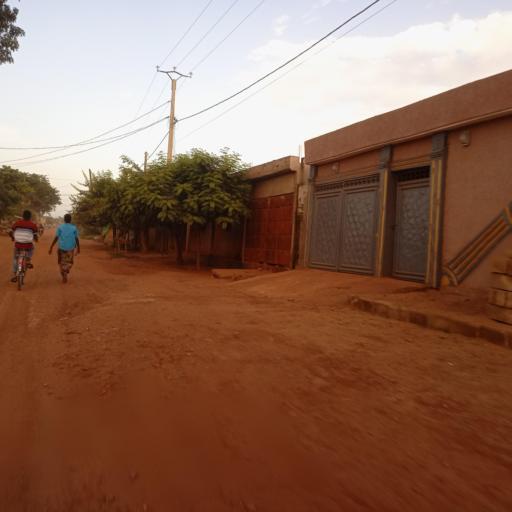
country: TG
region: Savanes
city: Dapaong
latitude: 10.8614
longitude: 0.1823
